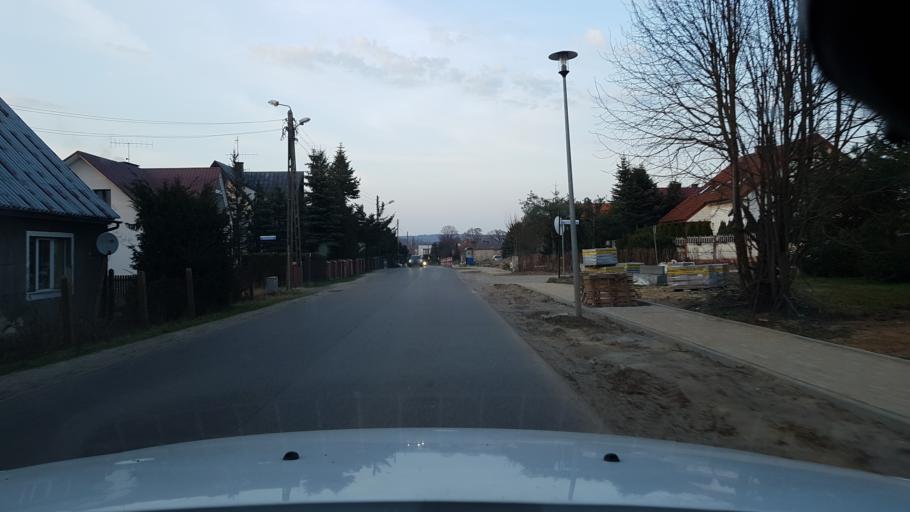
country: PL
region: West Pomeranian Voivodeship
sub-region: Koszalin
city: Koszalin
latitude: 54.1574
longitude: 16.2129
